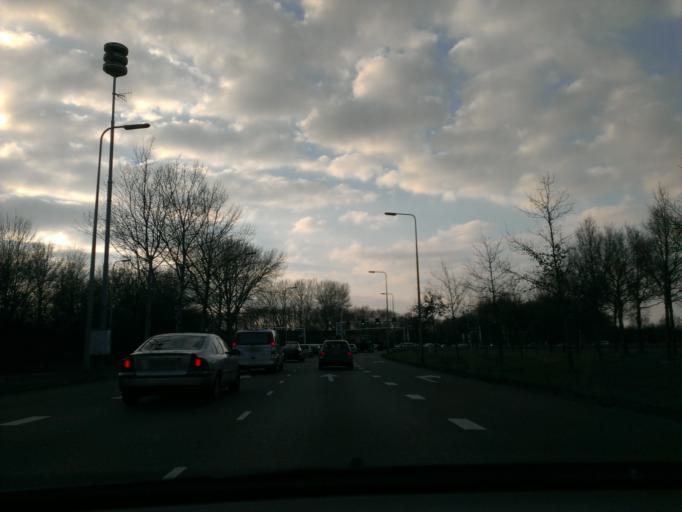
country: NL
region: Overijssel
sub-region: Gemeente Zwolle
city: Zwolle
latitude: 52.4929
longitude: 6.1160
